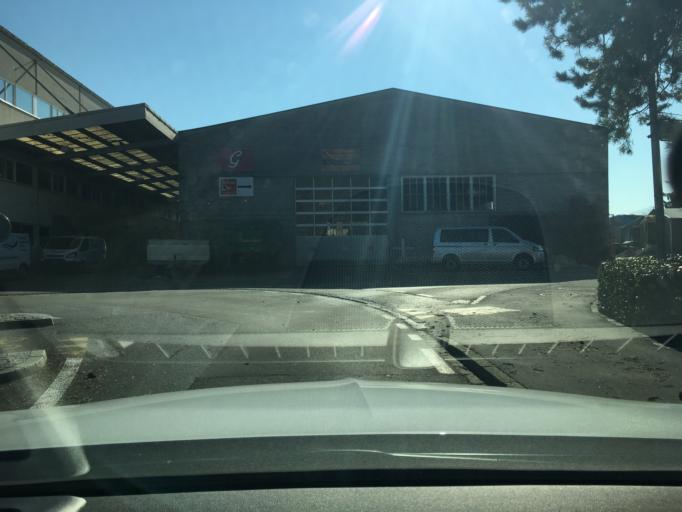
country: CH
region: Appenzell Innerrhoden
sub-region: Appenzell Inner Rhodes
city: Balgach
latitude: 47.4069
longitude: 9.6175
